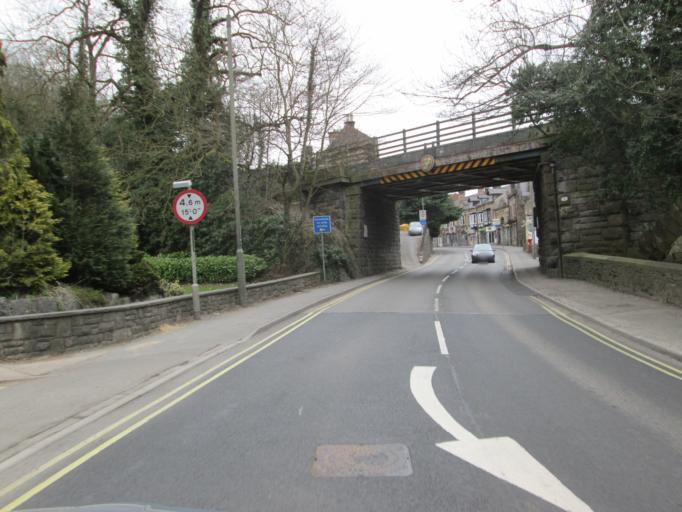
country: GB
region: England
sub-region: Derbyshire
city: Matlock
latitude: 53.1349
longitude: -1.5569
